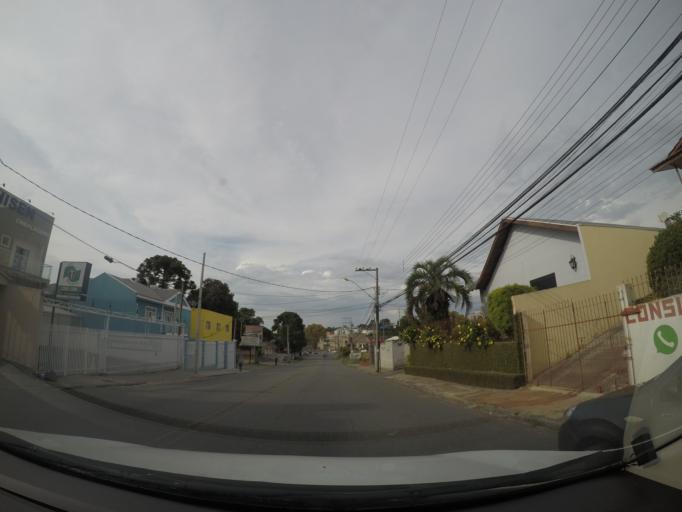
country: BR
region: Parana
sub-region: Sao Jose Dos Pinhais
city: Sao Jose dos Pinhais
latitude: -25.4880
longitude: -49.2247
